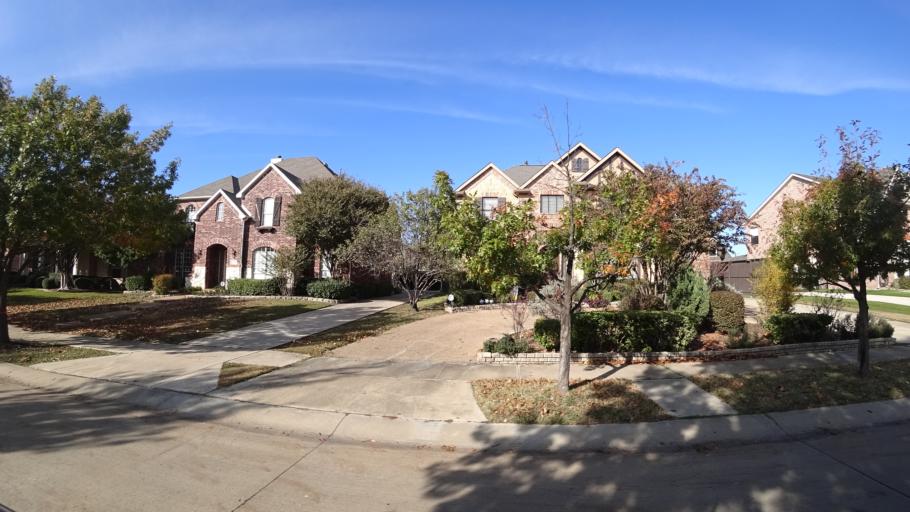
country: US
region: Texas
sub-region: Denton County
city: The Colony
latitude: 33.0286
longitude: -96.8961
